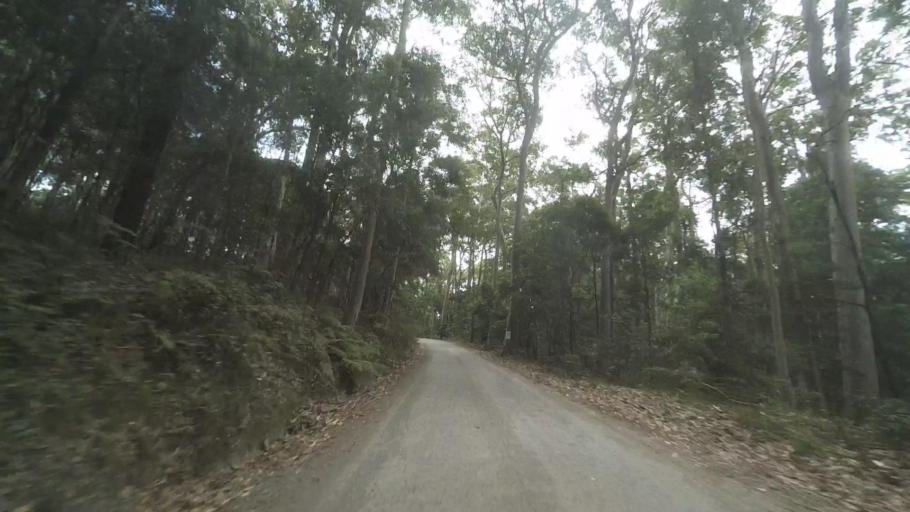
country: AU
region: New South Wales
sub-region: Shoalhaven Shire
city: Milton
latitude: -35.4405
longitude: 150.3146
